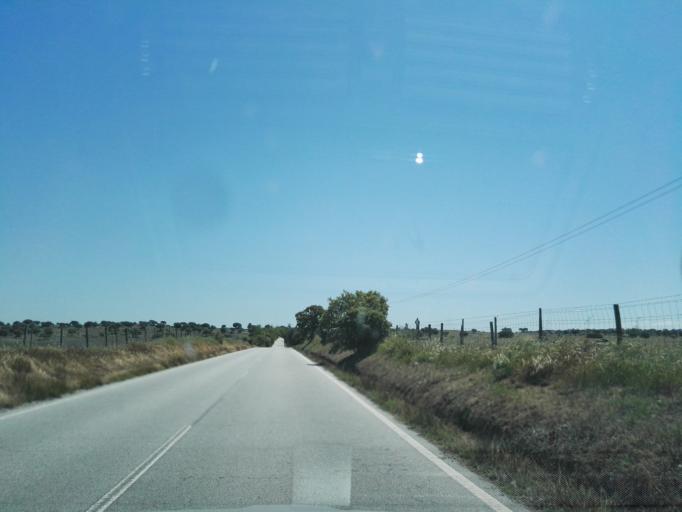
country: PT
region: Portalegre
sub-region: Arronches
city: Arronches
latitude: 39.0081
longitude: -7.2366
